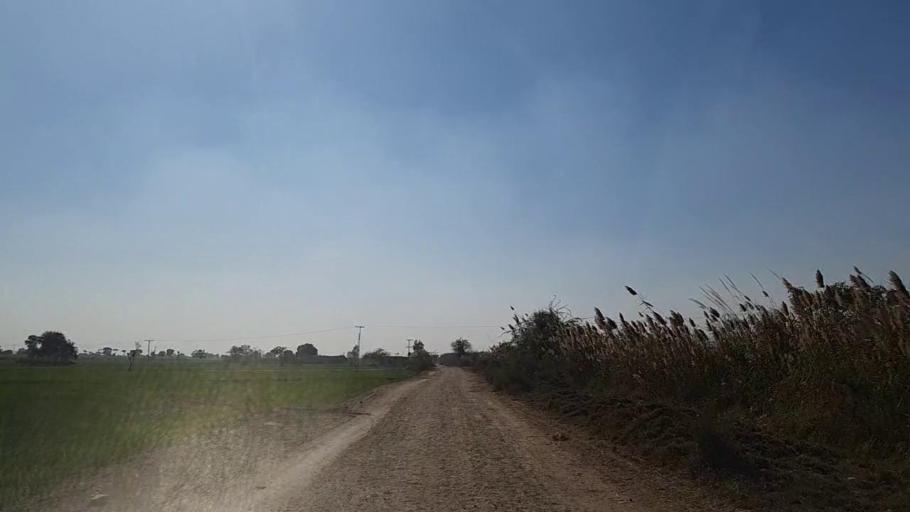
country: PK
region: Sindh
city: Bandhi
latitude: 26.5214
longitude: 68.2864
